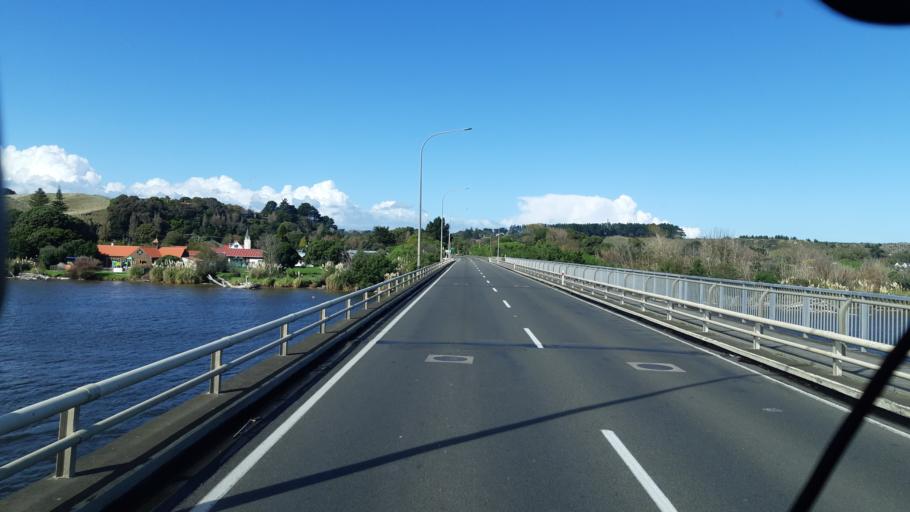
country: NZ
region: Manawatu-Wanganui
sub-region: Wanganui District
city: Wanganui
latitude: -39.9450
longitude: 175.0461
